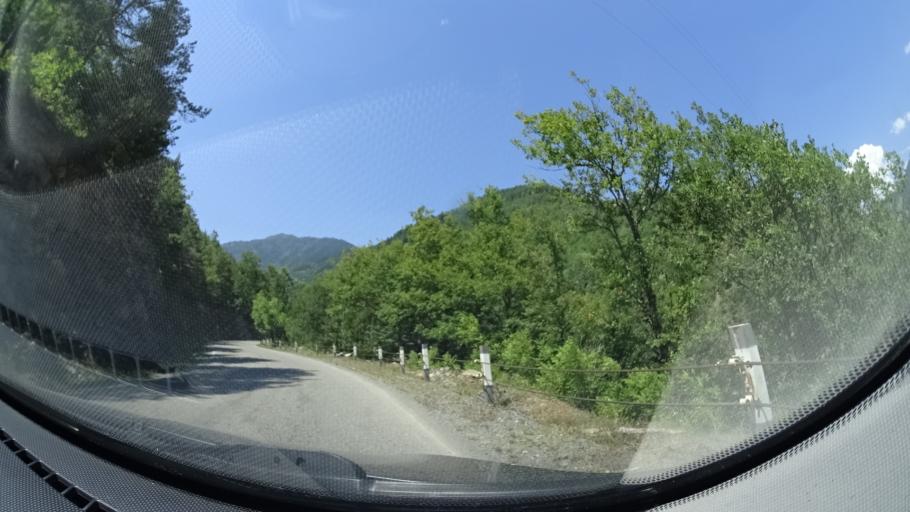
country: GE
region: Ajaria
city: Khulo
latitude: 41.6252
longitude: 42.2850
